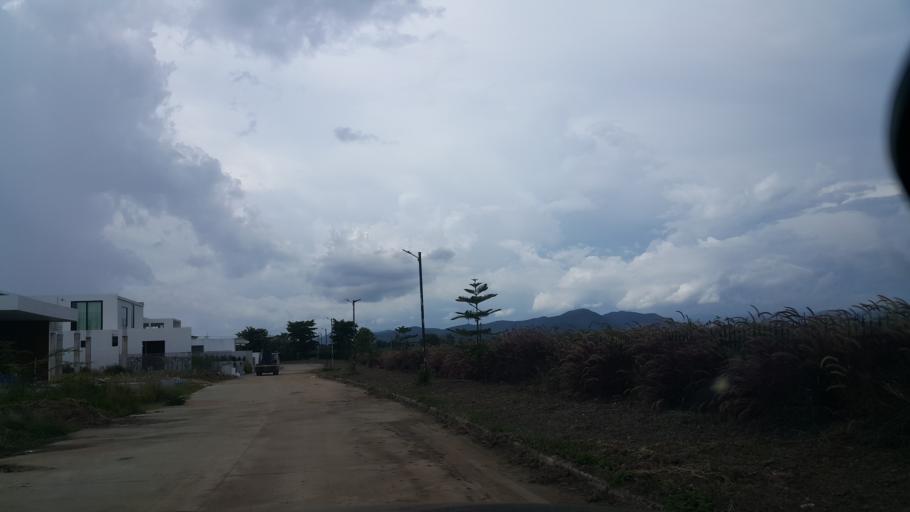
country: TH
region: Chiang Mai
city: San Kamphaeng
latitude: 18.7192
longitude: 99.1572
